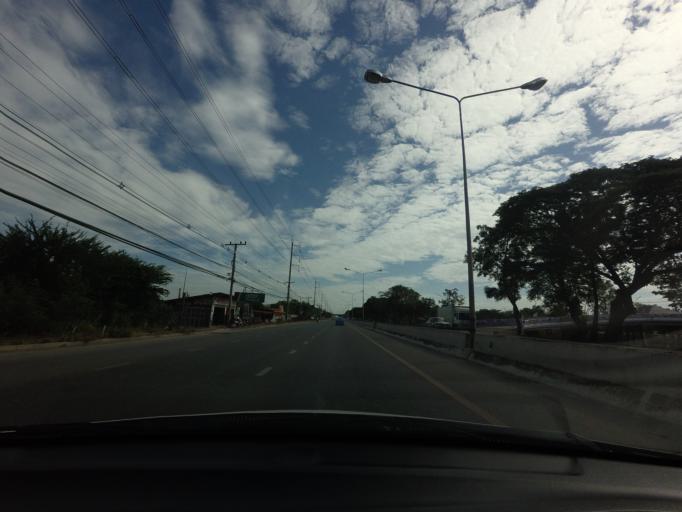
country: TH
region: Pathum Thani
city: Nong Suea
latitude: 14.0587
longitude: 100.8412
